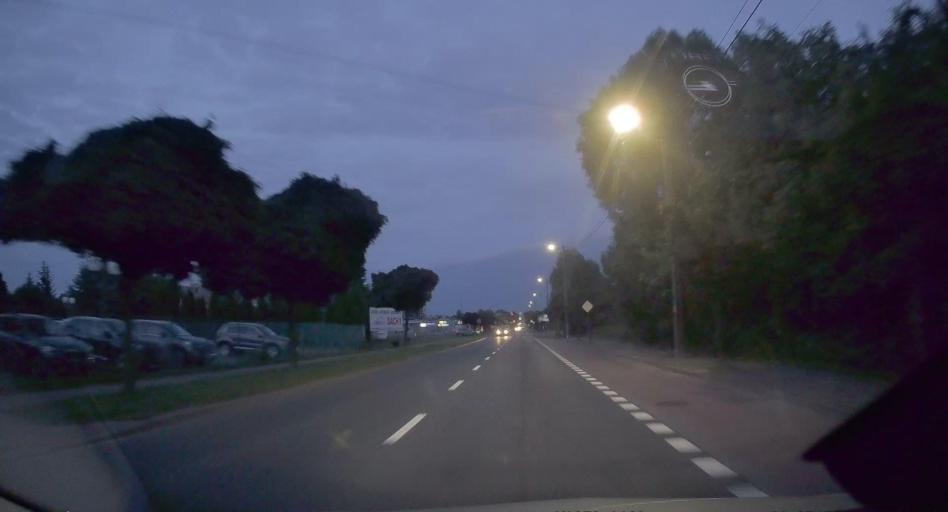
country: PL
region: Silesian Voivodeship
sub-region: Powiat klobucki
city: Klobuck
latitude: 50.9037
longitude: 18.9279
